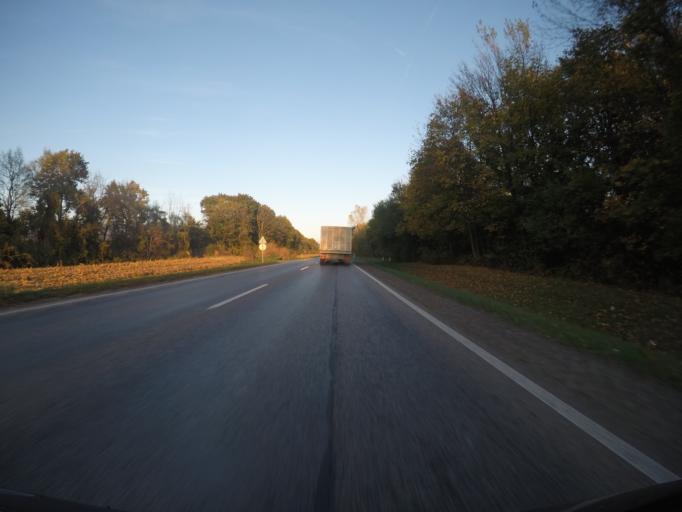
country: HU
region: Baranya
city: Pellerd
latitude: 46.0584
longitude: 18.1053
